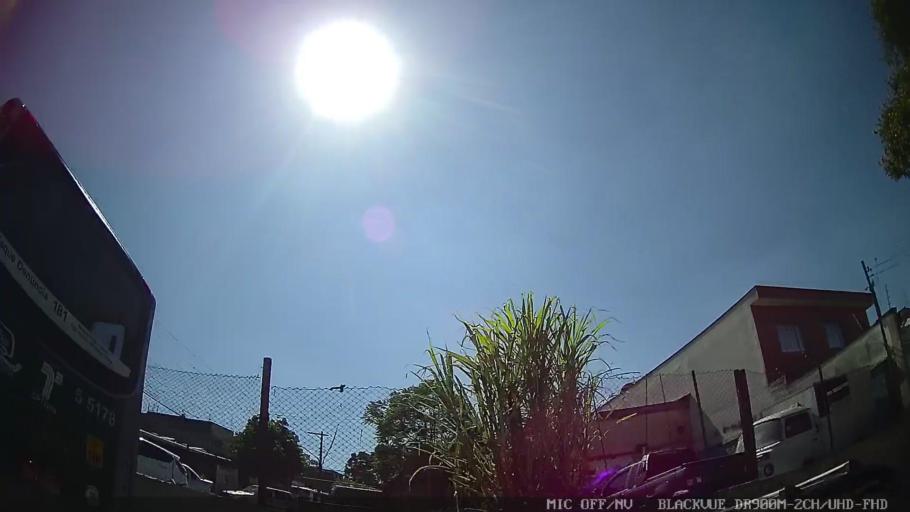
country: BR
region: Sao Paulo
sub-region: Sao Caetano Do Sul
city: Sao Caetano do Sul
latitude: -23.5936
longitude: -46.4980
